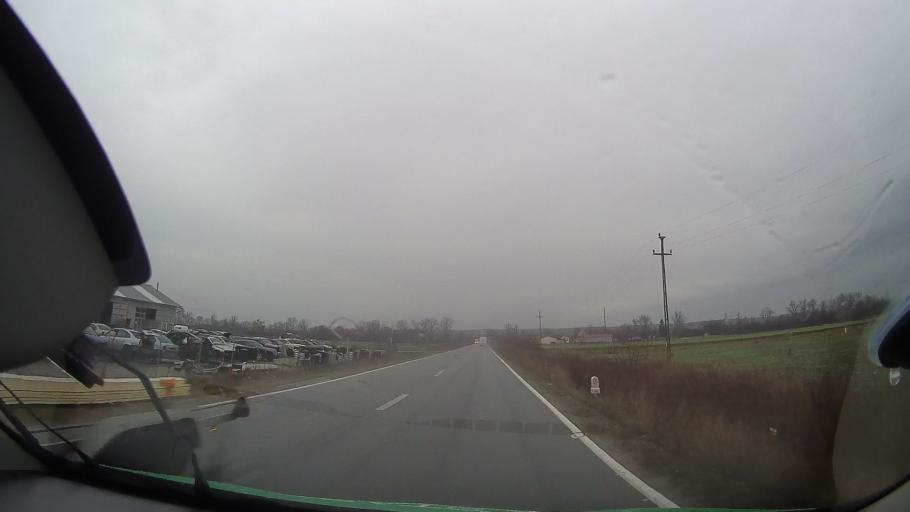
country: RO
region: Bihor
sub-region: Comuna Tinca
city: Tinca
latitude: 46.7642
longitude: 21.9340
